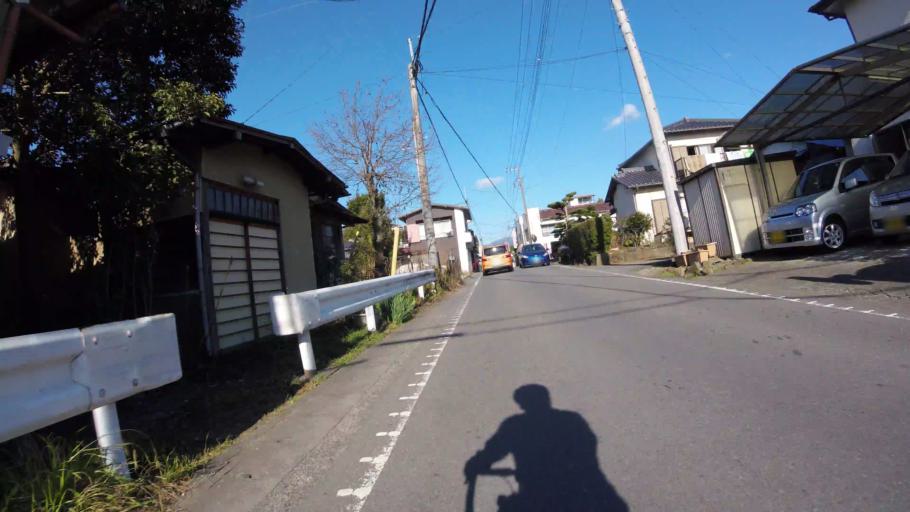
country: JP
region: Shizuoka
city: Mishima
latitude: 35.0794
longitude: 138.9669
